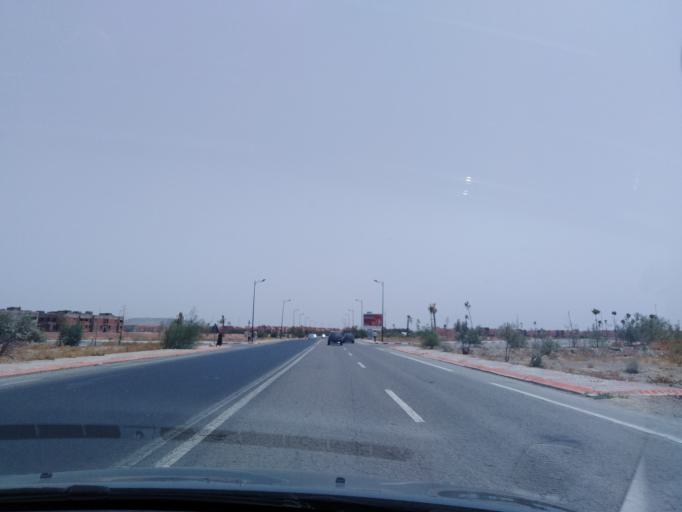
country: MA
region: Marrakech-Tensift-Al Haouz
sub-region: Marrakech
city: Marrakesh
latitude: 31.7672
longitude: -8.1220
